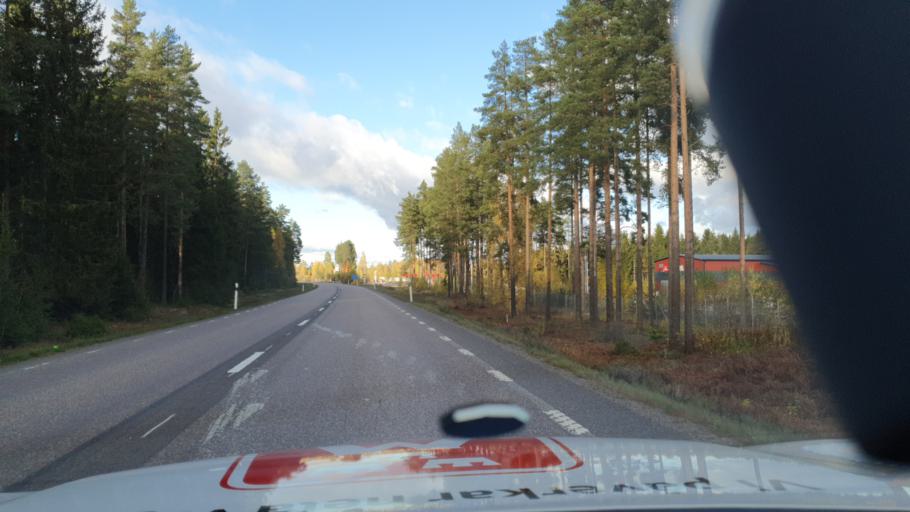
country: SE
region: Gaevleborg
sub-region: Gavle Kommun
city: Hedesunda
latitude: 60.3900
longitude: 16.9766
